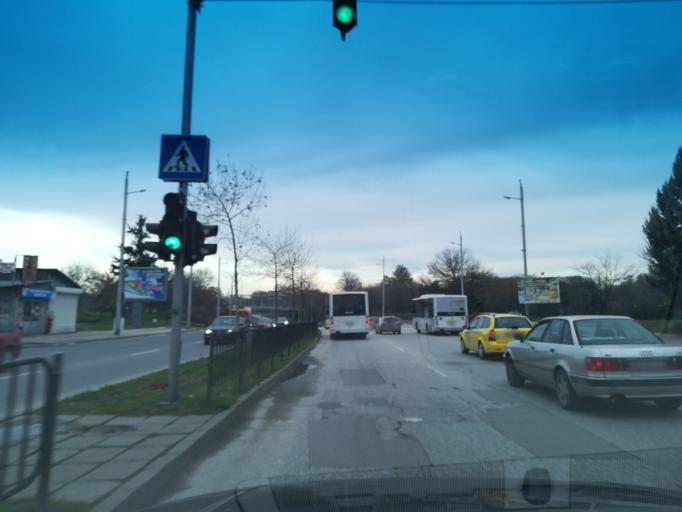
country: BG
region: Plovdiv
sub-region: Obshtina Plovdiv
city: Plovdiv
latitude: 42.1333
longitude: 24.7306
